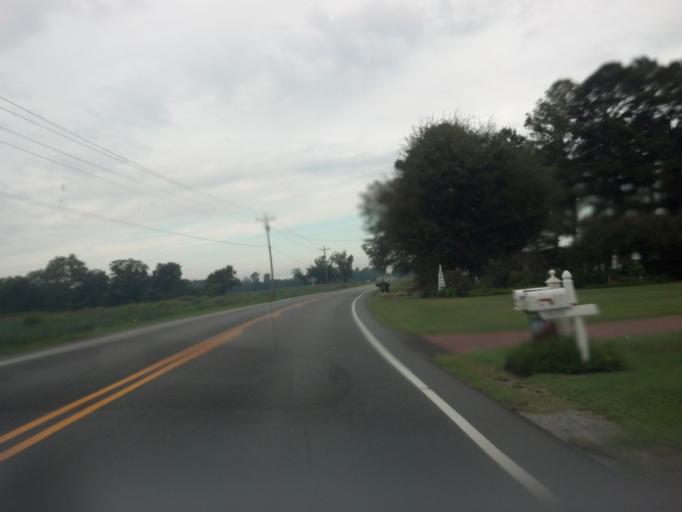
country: US
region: North Carolina
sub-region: Pitt County
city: Ayden
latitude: 35.4567
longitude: -77.4897
